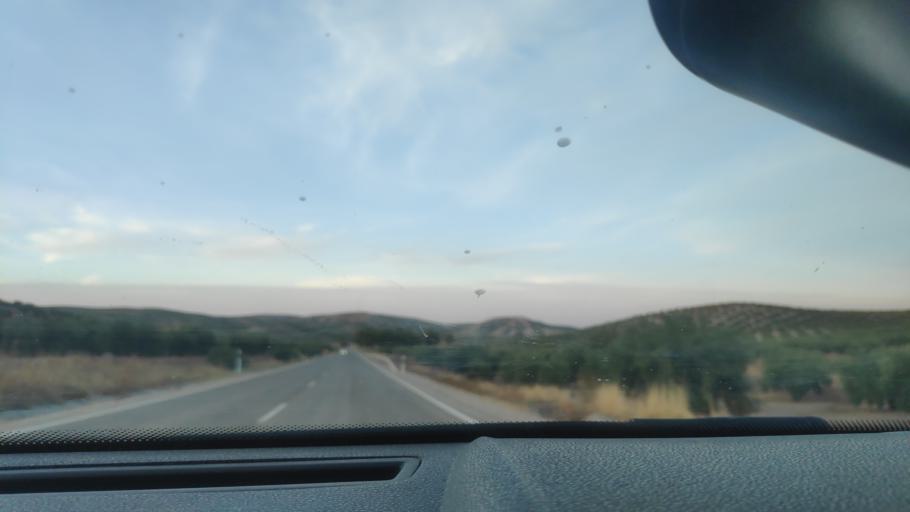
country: ES
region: Andalusia
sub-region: Provincia de Jaen
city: Escanuela
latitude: 37.8480
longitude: -4.0449
